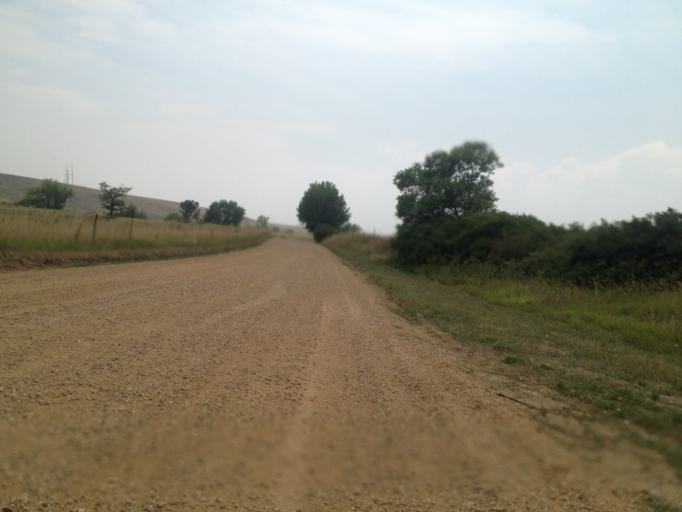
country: US
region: Colorado
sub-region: Boulder County
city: Superior
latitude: 39.9499
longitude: -105.1842
